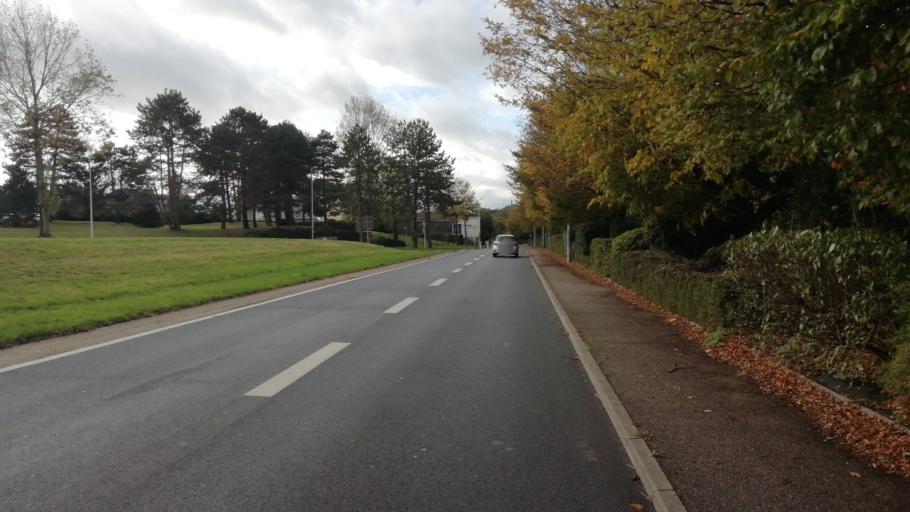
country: FR
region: Haute-Normandie
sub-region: Departement de la Seine-Maritime
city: Sainte-Adresse
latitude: 49.5179
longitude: 0.0869
